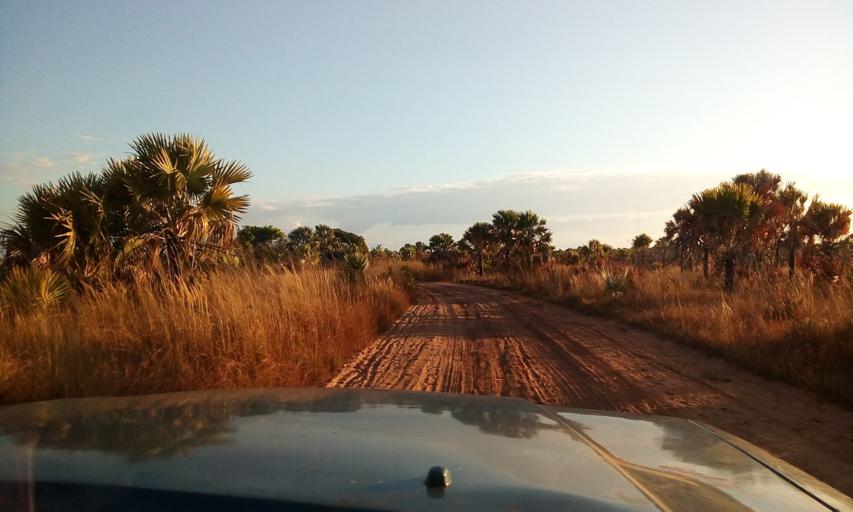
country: MG
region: Boeny
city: Sitampiky
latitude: -16.1203
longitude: 45.4616
